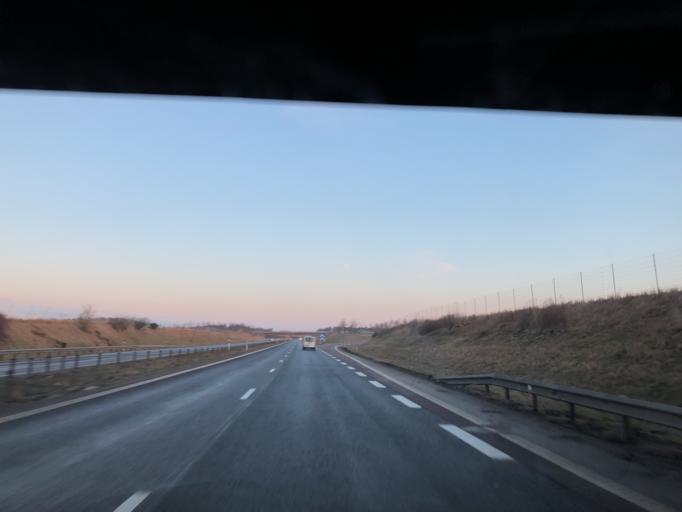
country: SE
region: Halland
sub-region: Laholms Kommun
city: Mellbystrand
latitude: 56.4485
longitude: 12.9519
